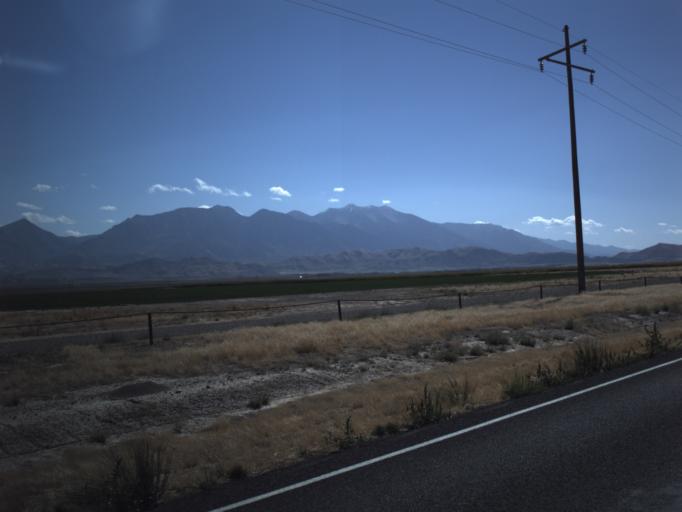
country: US
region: Utah
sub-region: Utah County
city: Genola
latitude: 40.0445
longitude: -111.9584
